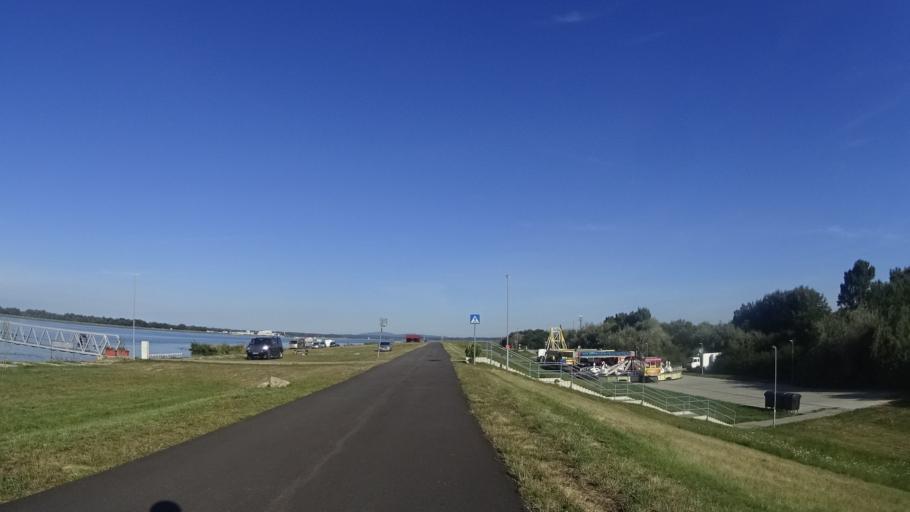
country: SK
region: Bratislavsky
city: Dunajska Luzna
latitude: 48.0320
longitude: 17.2508
